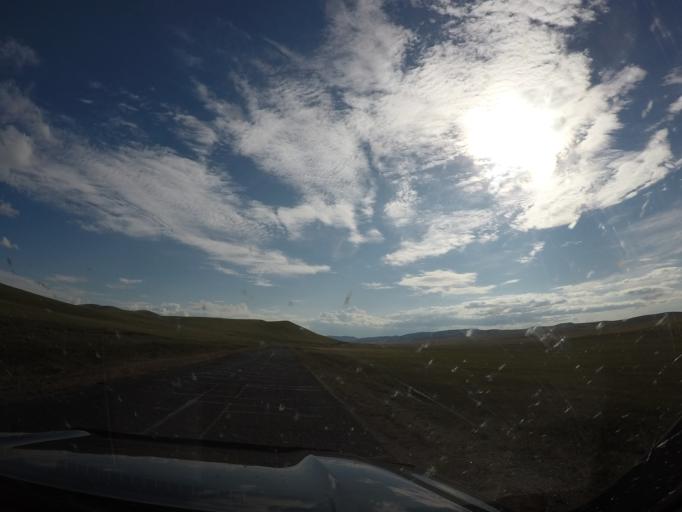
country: MN
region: Hentiy
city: Modot
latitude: 47.7704
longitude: 108.6512
